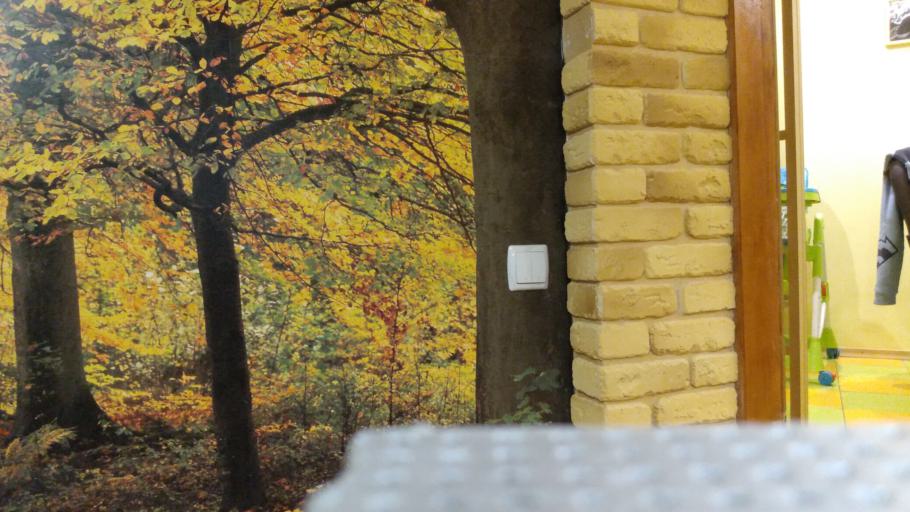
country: RU
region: Vologda
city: Babayevo
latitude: 59.3670
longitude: 35.9977
